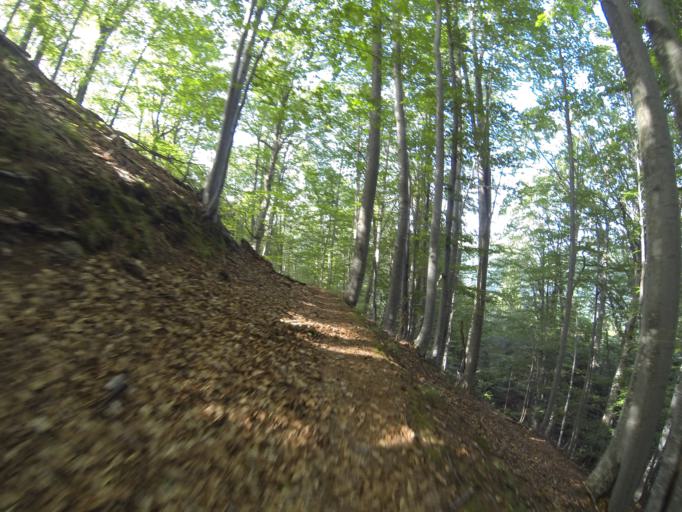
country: RO
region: Valcea
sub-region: Comuna Barbatesti
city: Barbatesti
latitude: 45.2552
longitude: 24.1553
